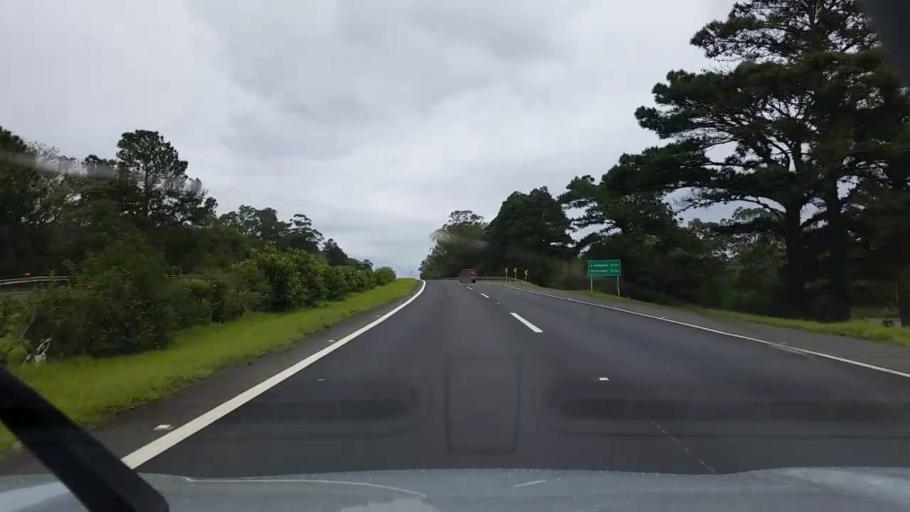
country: BR
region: Rio Grande do Sul
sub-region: Osorio
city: Osorio
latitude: -29.8890
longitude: -50.2785
